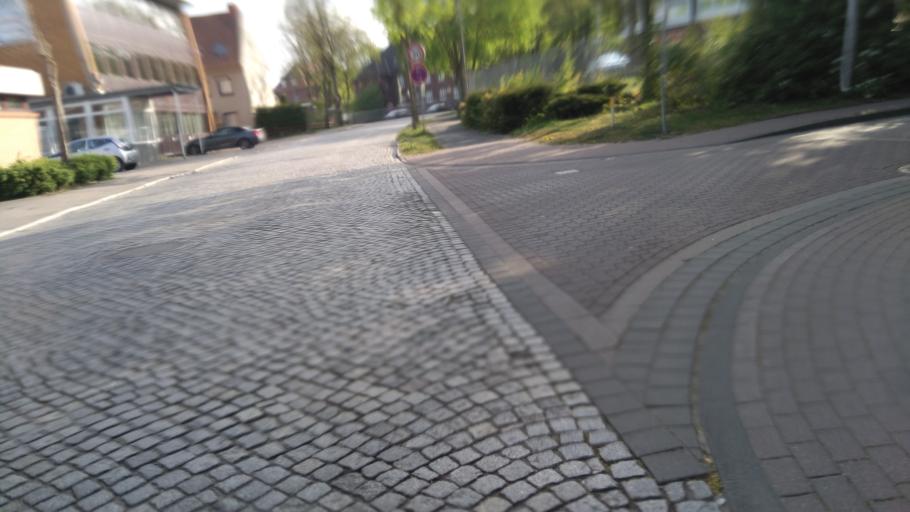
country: DE
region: Lower Saxony
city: Buxtehude
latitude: 53.4627
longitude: 9.6892
